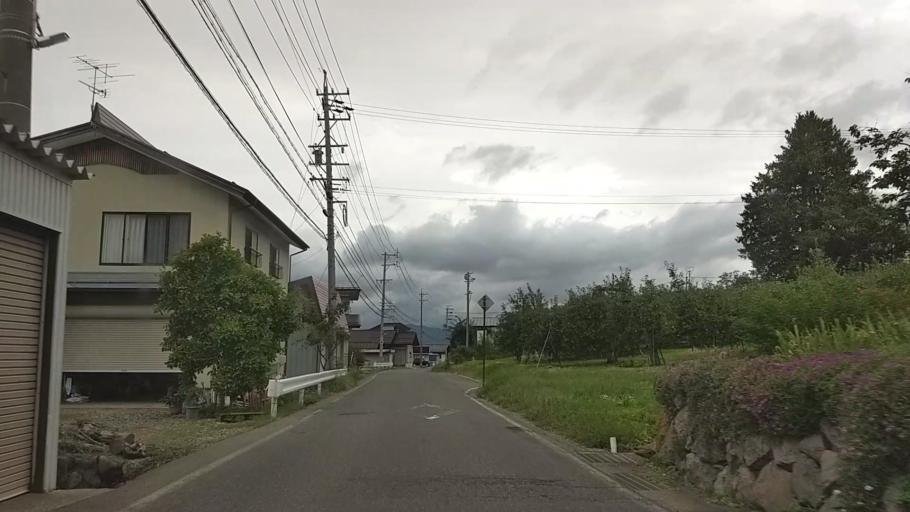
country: JP
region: Nagano
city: Iiyama
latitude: 36.8016
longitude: 138.3590
